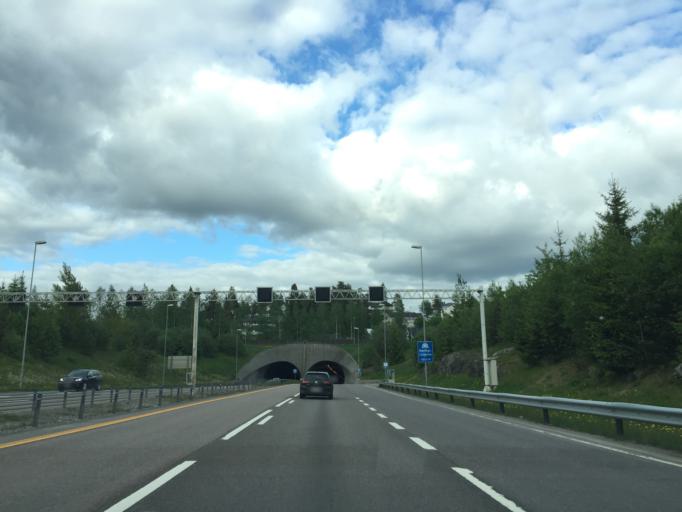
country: NO
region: Akershus
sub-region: Skedsmo
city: Lillestrom
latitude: 59.9394
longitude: 11.0123
